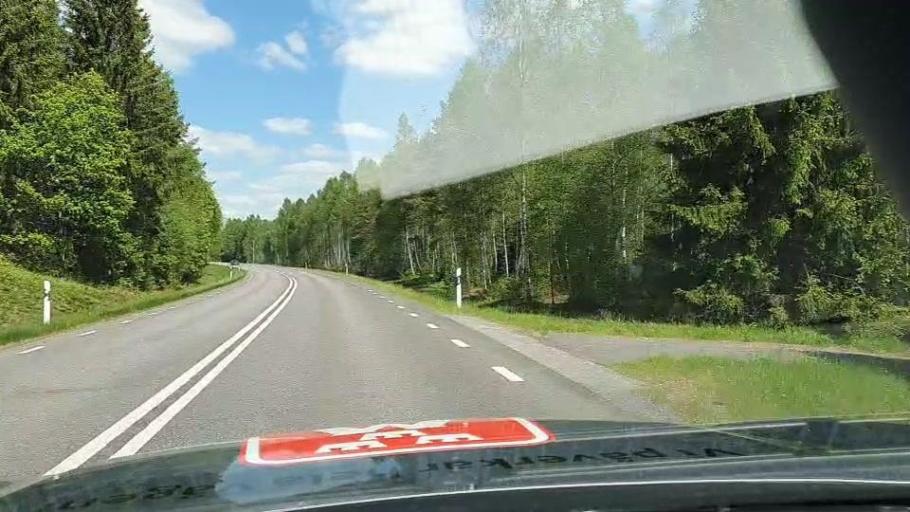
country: SE
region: Kronoberg
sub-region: Alvesta Kommun
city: Moheda
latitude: 57.0389
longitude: 14.5653
